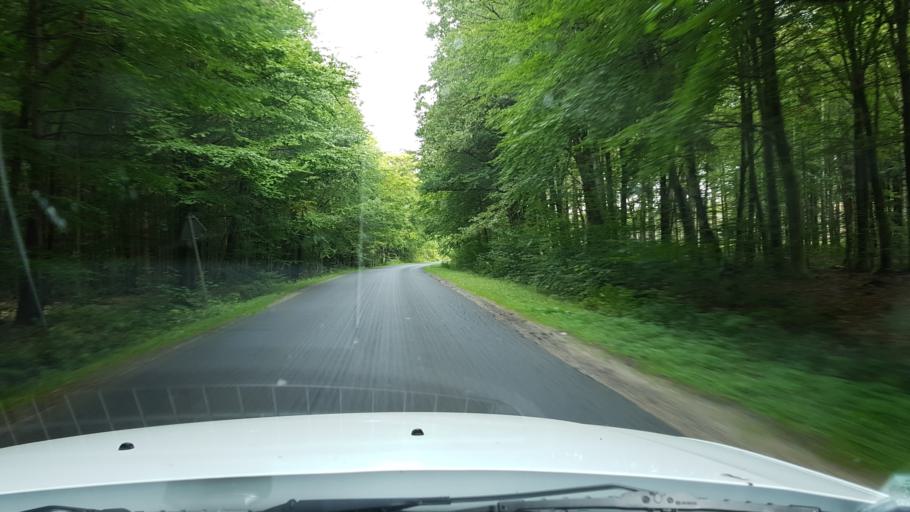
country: PL
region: West Pomeranian Voivodeship
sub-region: Powiat slawienski
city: Slawno
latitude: 54.4025
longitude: 16.6159
